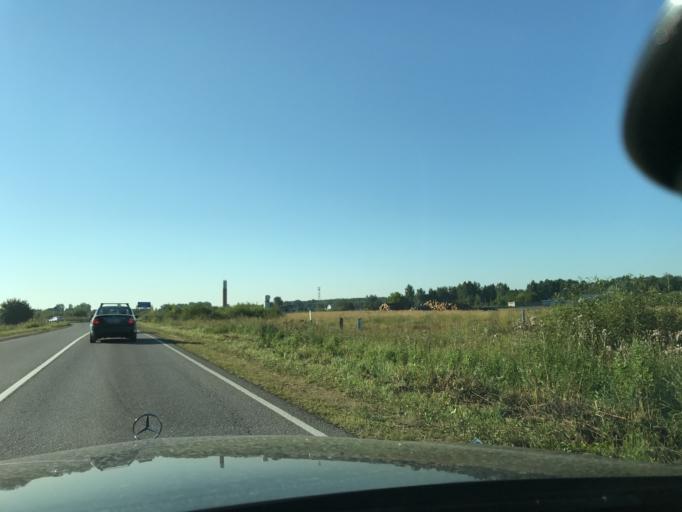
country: RU
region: Moskovskaya
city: Bakhchivandzhi
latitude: 55.8501
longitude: 38.0817
